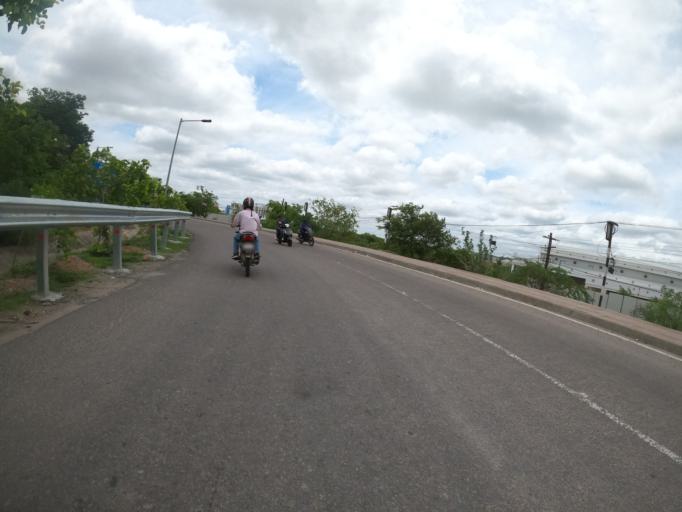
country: IN
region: Telangana
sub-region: Hyderabad
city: Hyderabad
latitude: 17.3851
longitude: 78.3537
